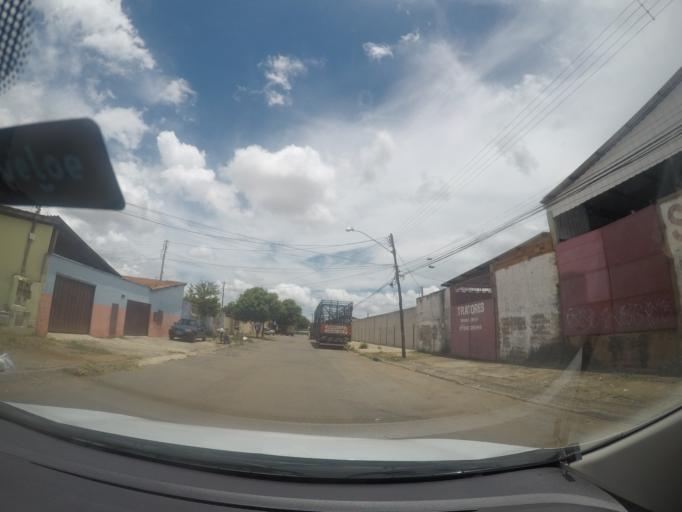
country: BR
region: Goias
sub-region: Goiania
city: Goiania
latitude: -16.6735
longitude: -49.3149
